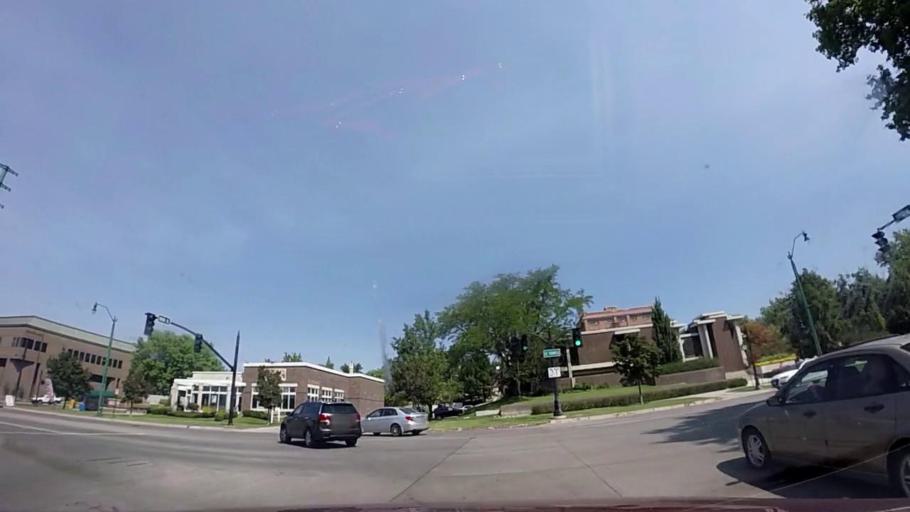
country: US
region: Utah
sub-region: Salt Lake County
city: Salt Lake City
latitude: 40.7692
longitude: -111.8768
